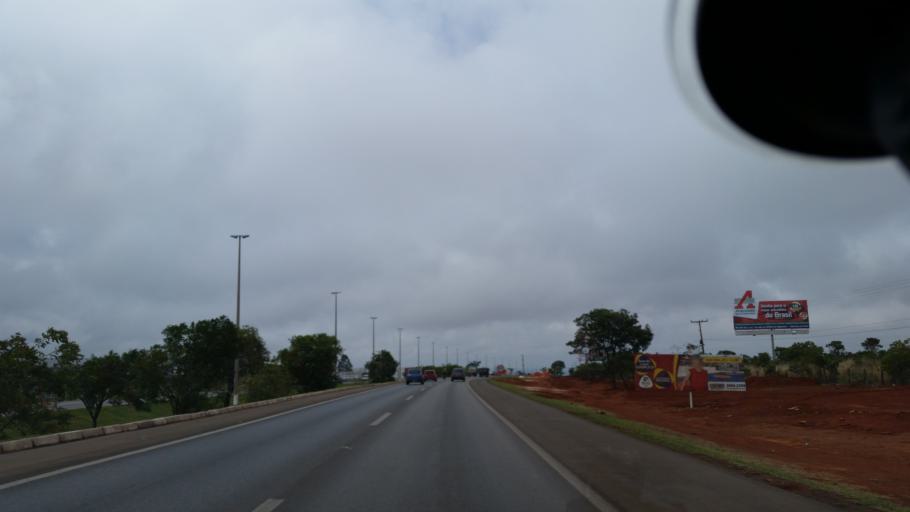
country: BR
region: Goias
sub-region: Luziania
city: Luziania
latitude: -16.0300
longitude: -47.9789
